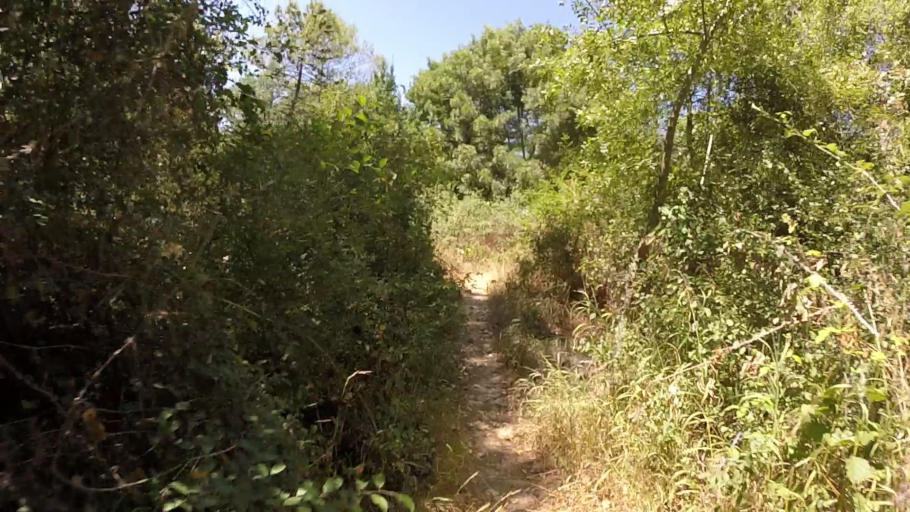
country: FR
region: Provence-Alpes-Cote d'Azur
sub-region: Departement des Alpes-Maritimes
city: Mougins
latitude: 43.6171
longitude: 7.0393
